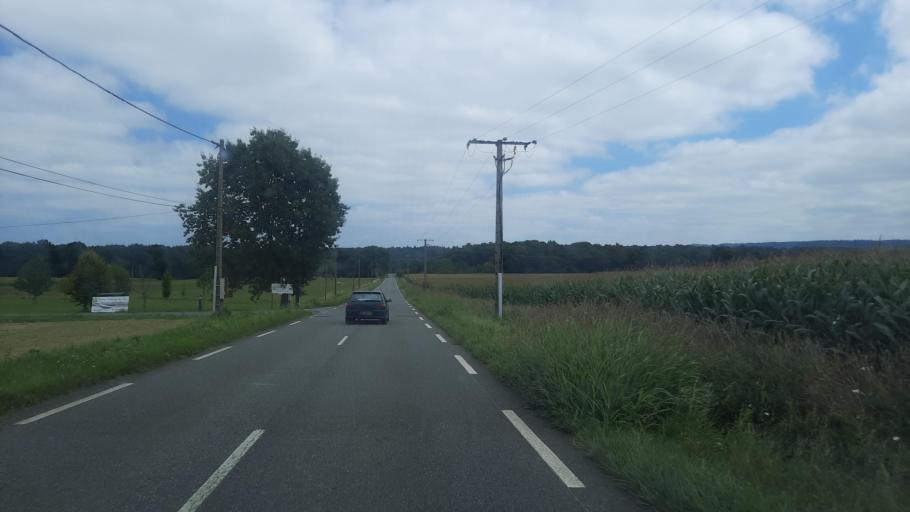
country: FR
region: Midi-Pyrenees
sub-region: Departement des Hautes-Pyrenees
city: Trie-sur-Baise
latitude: 43.3002
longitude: 0.4128
